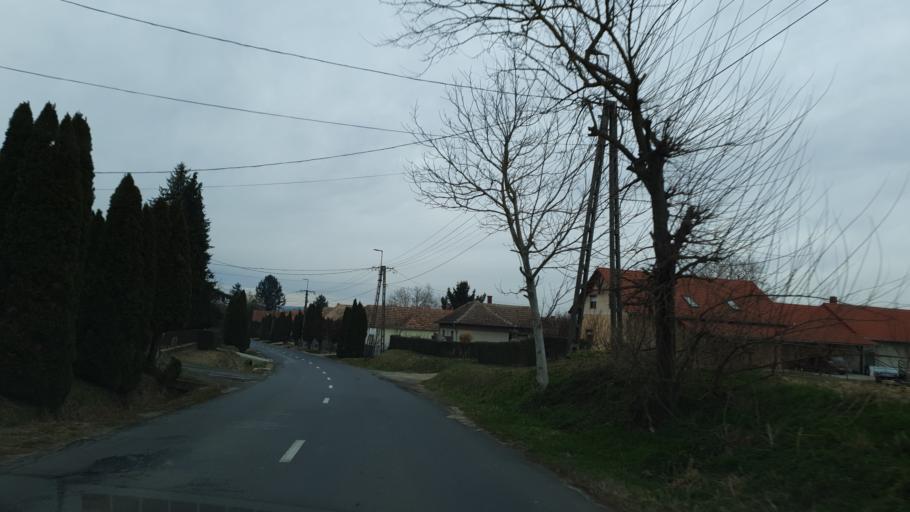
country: HU
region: Zala
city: Sarmellek
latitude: 46.7220
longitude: 17.1068
